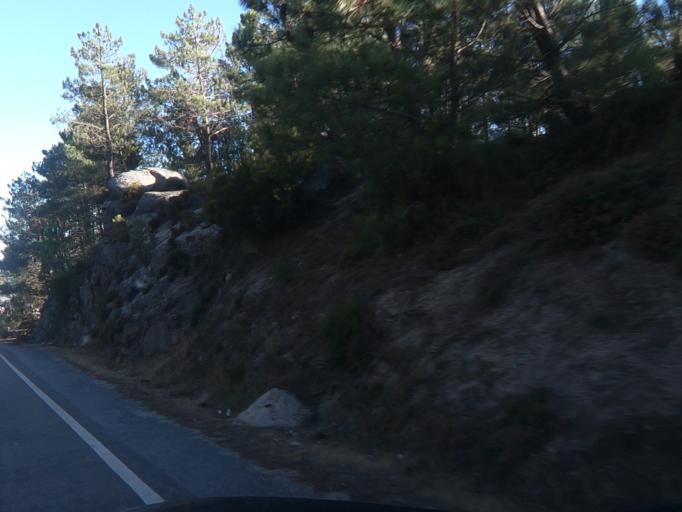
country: PT
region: Vila Real
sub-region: Vila Real
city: Vila Real
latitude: 41.3343
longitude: -7.7882
